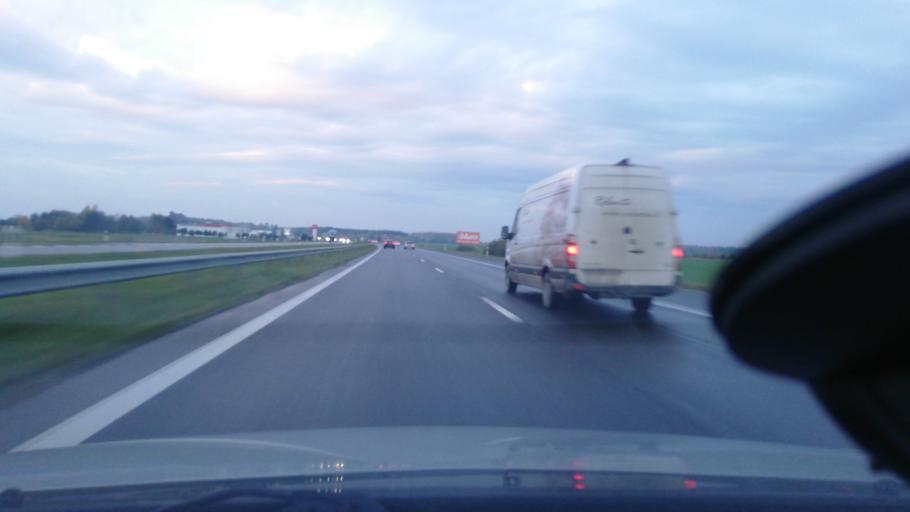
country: LT
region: Klaipedos apskritis
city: Gargzdai
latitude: 55.7324
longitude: 21.3817
